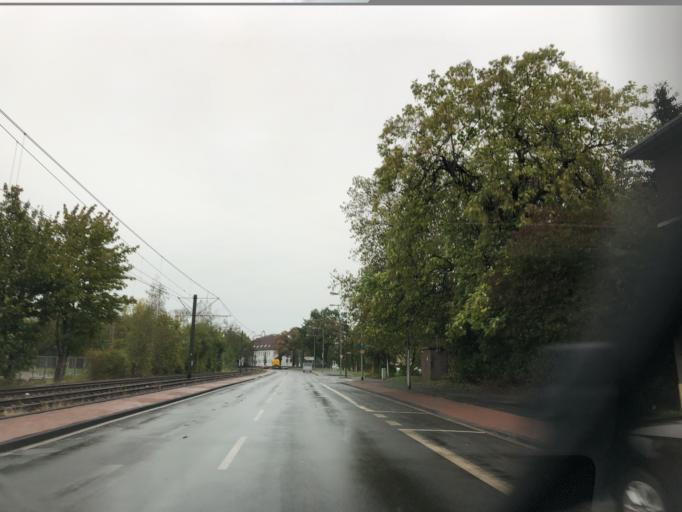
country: DE
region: North Rhine-Westphalia
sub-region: Regierungsbezirk Dusseldorf
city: Hochfeld
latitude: 51.3698
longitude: 6.7306
